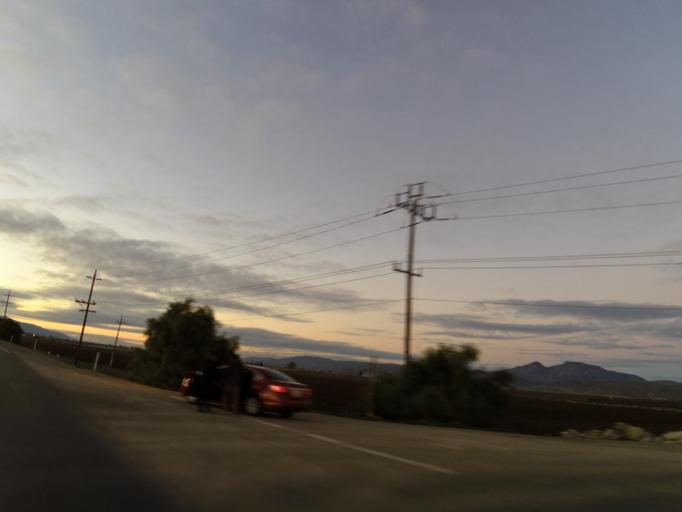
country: US
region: California
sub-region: Monterey County
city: Greenfield
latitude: 36.2938
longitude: -121.2009
